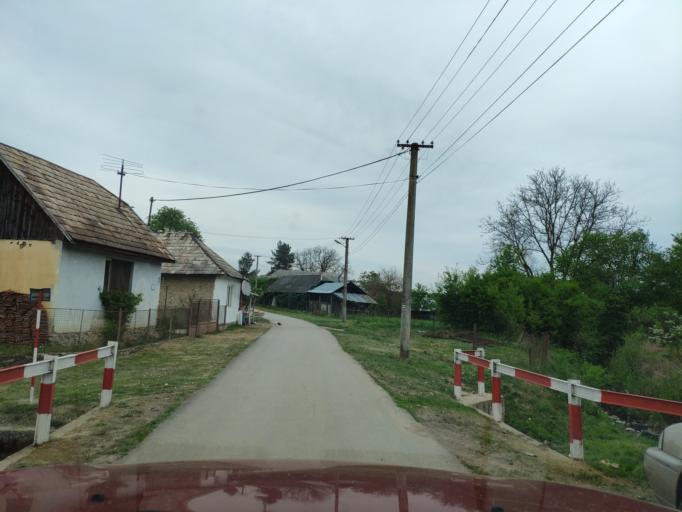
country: SK
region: Banskobystricky
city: Revuca
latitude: 48.5142
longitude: 20.1726
